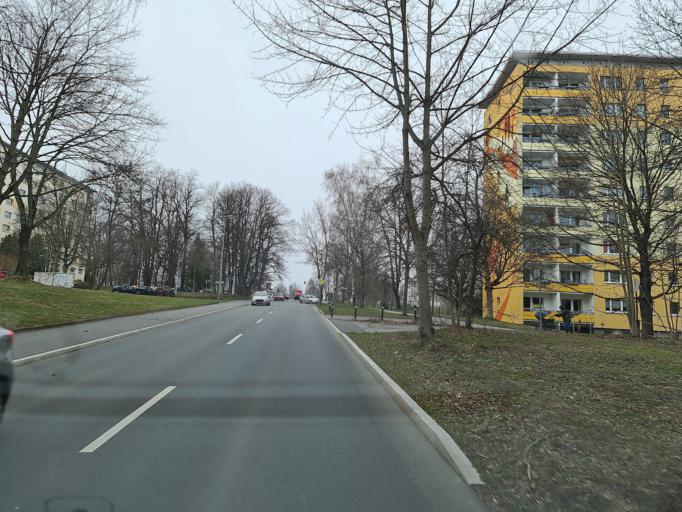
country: DE
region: Saxony
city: Neukirchen
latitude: 50.8042
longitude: 12.8907
